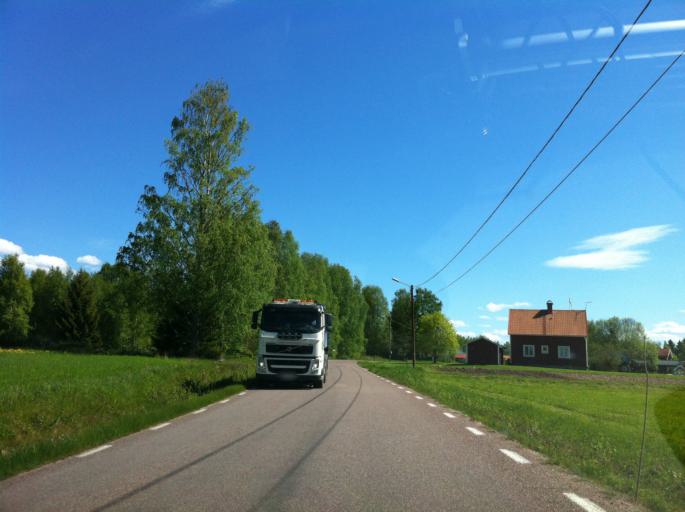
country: SE
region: Dalarna
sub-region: Mora Kommun
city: Mora
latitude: 60.9791
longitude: 14.6339
